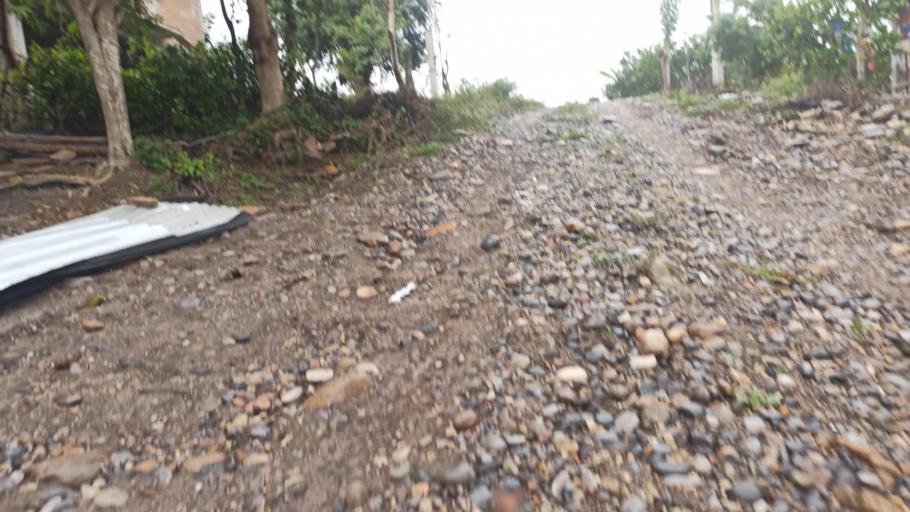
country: MX
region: Veracruz
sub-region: Papantla
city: El Chote
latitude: 20.3602
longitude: -97.3426
